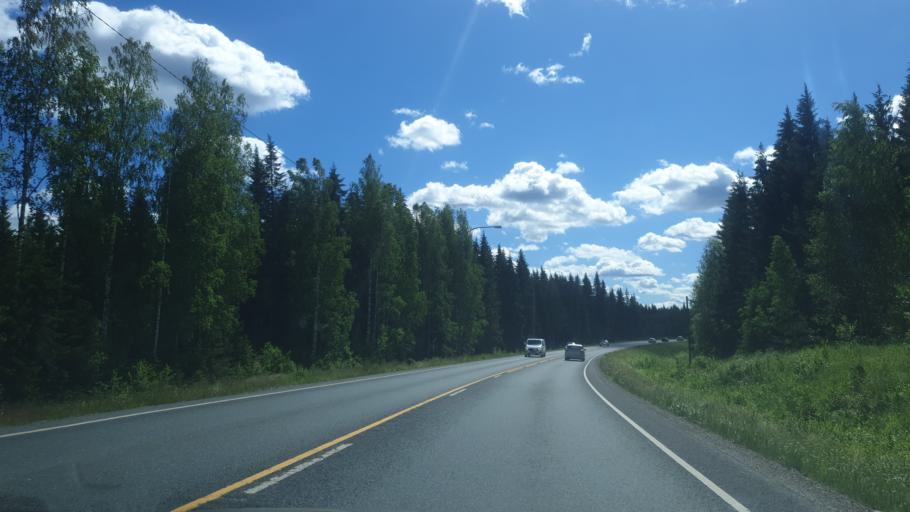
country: FI
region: Northern Savo
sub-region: Varkaus
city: Leppaevirta
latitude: 62.5652
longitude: 27.6195
